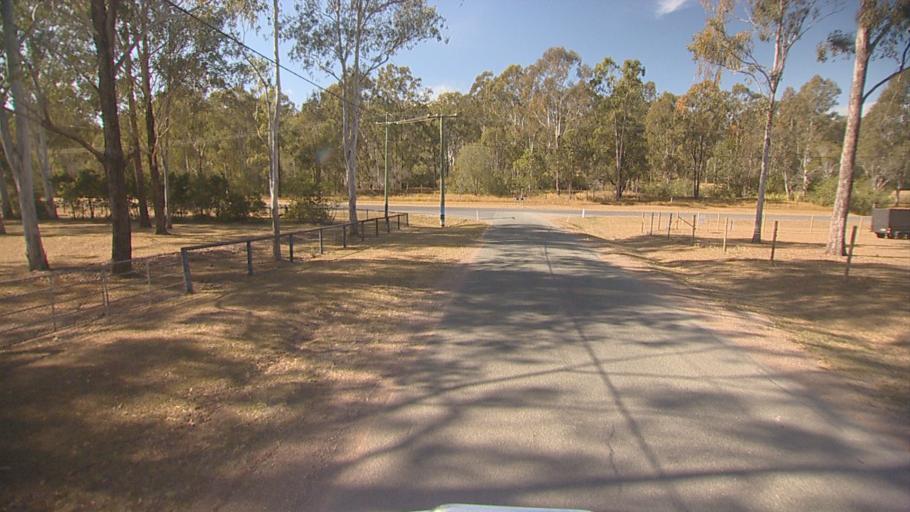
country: AU
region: Queensland
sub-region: Logan
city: Cedar Vale
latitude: -27.8634
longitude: 152.9768
